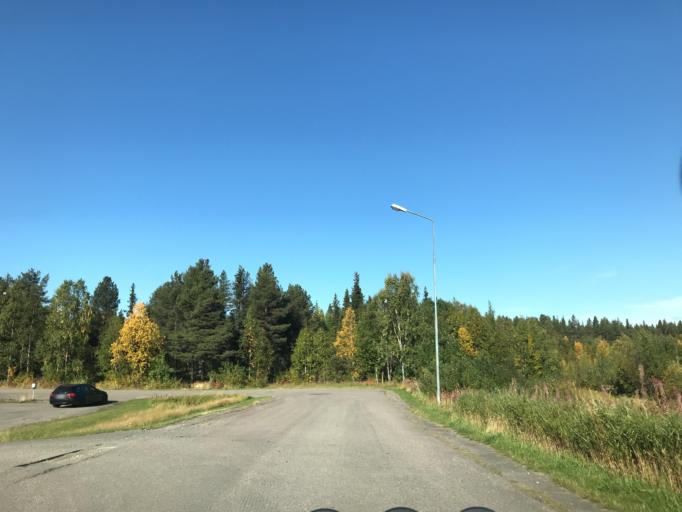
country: SE
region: Norrbotten
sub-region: Gallivare Kommun
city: Malmberget
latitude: 67.6500
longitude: 21.0583
